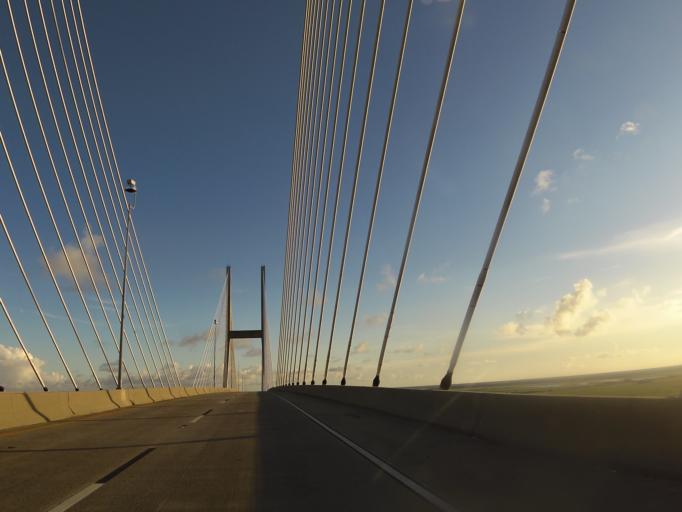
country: US
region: Georgia
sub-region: Glynn County
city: Brunswick
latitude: 31.1175
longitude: -81.4846
